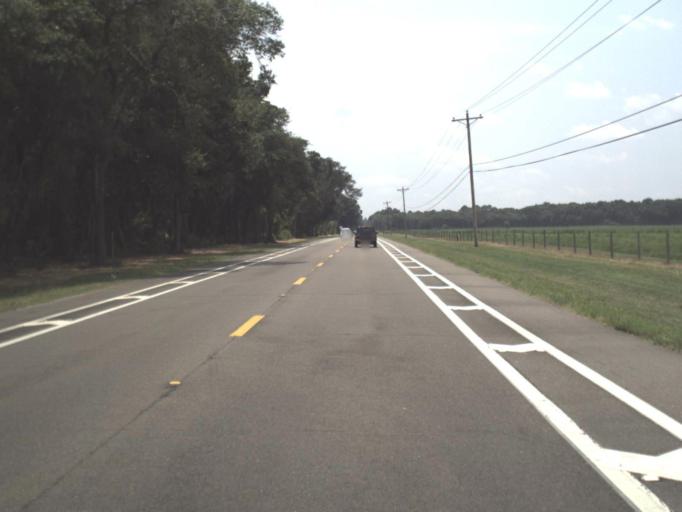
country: US
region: Florida
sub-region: Levy County
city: Manatee Road
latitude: 29.4963
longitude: -82.9450
